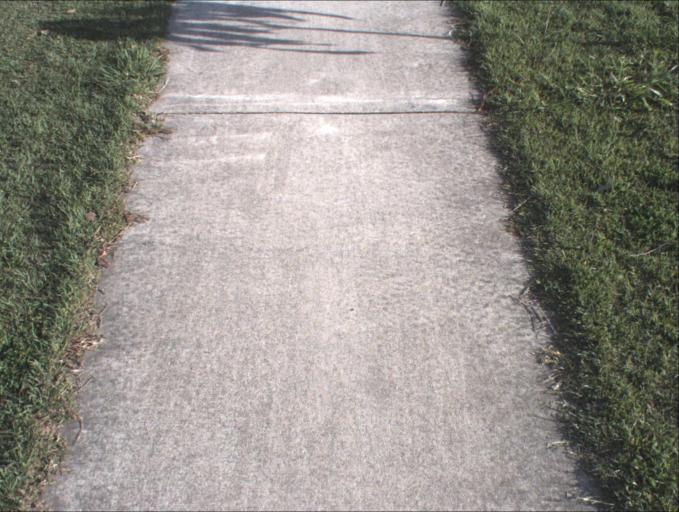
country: AU
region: Queensland
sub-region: Logan
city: Logan Reserve
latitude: -27.6984
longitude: 153.0944
